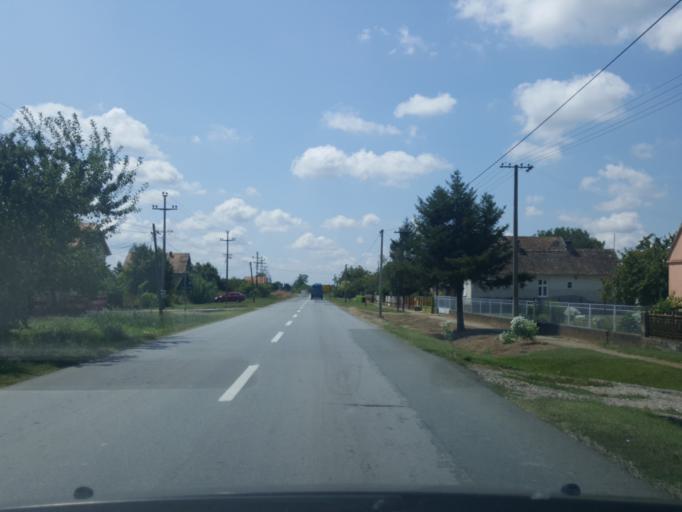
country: RS
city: Salas Nocajski
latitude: 44.9432
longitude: 19.5785
